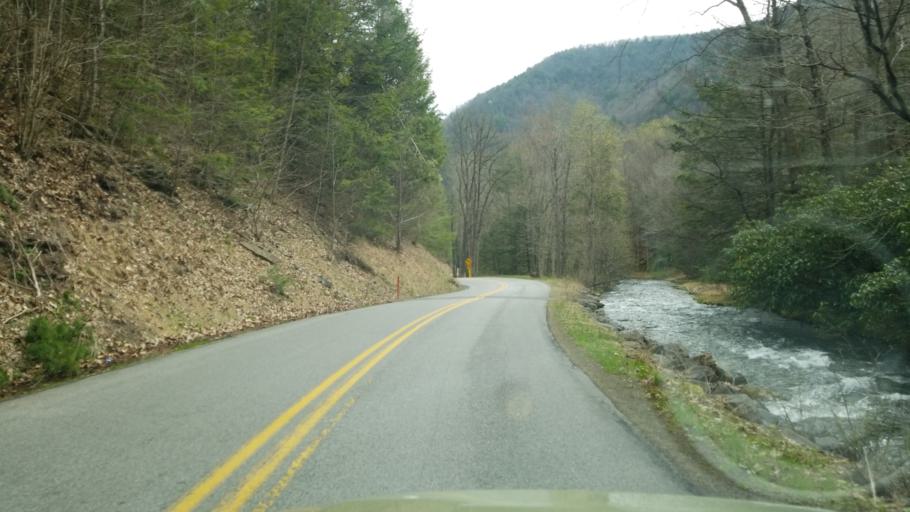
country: US
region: Pennsylvania
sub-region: Cameron County
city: Emporium
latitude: 41.2893
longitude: -78.1215
